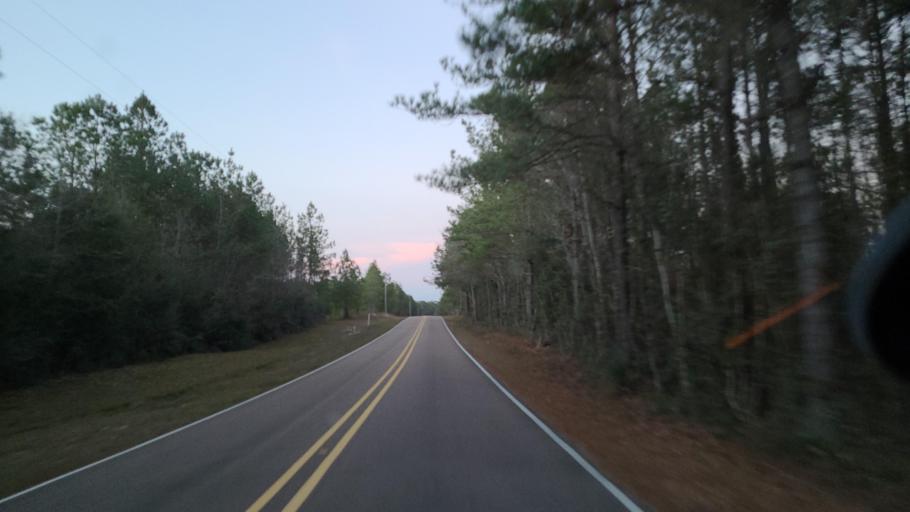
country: US
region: Mississippi
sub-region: Forrest County
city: Hattiesburg
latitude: 31.2200
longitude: -89.2369
